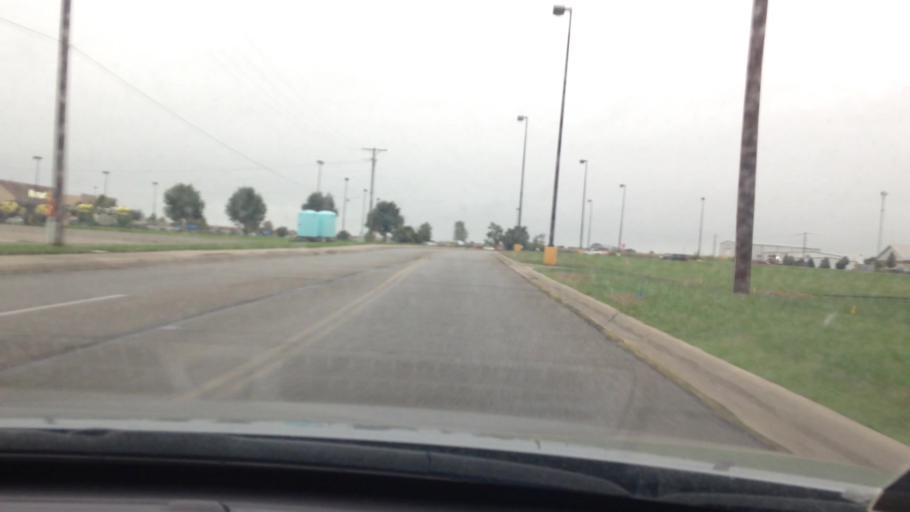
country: US
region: Kansas
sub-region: Brown County
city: Hiawatha
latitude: 39.8483
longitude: -95.5617
